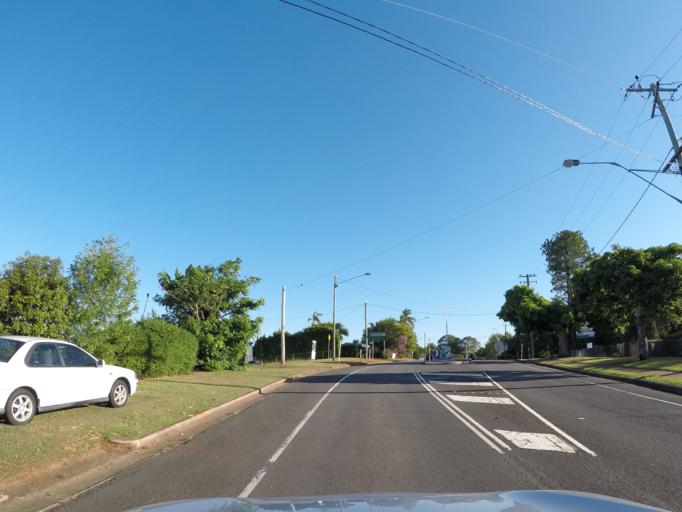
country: AU
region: Queensland
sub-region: Sunshine Coast
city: Nambour
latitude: -26.6249
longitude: 152.8665
